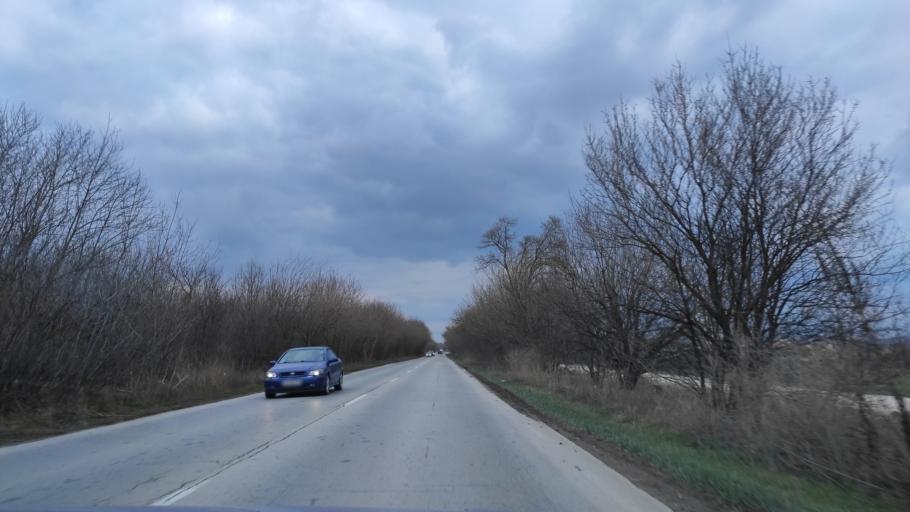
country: BG
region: Varna
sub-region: Obshtina Aksakovo
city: Aksakovo
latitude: 43.2286
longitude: 27.8377
